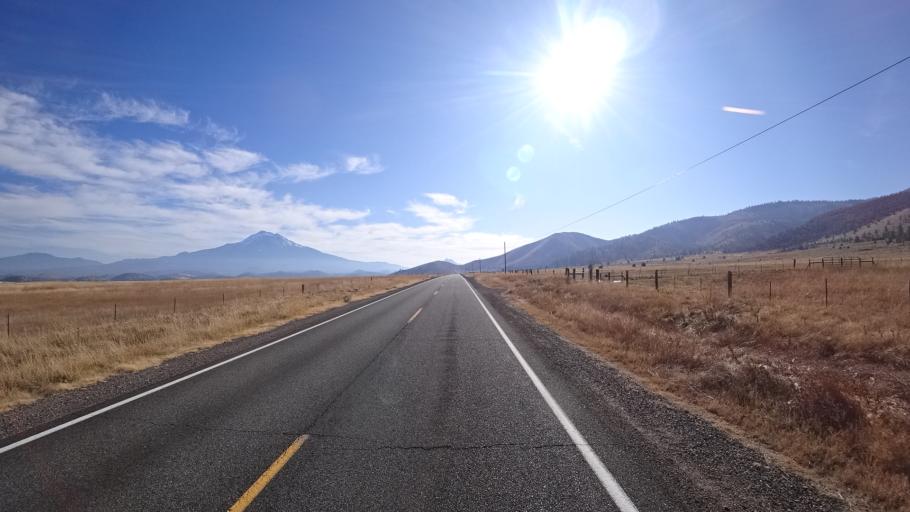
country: US
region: California
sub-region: Siskiyou County
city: Weed
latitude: 41.4842
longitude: -122.4981
